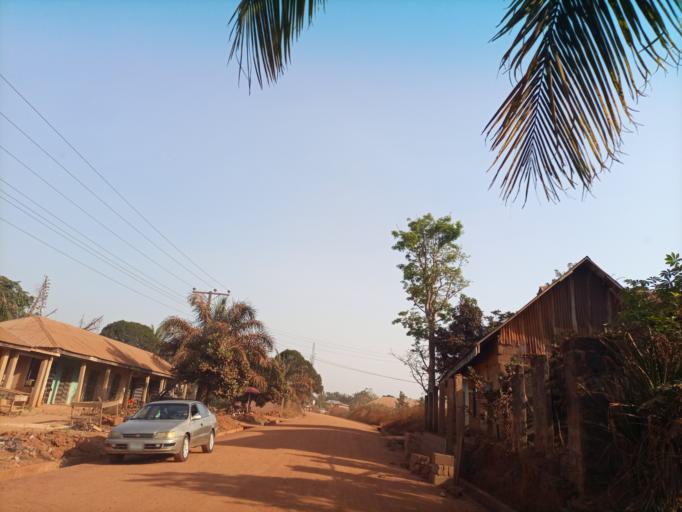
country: NG
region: Enugu
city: Opi
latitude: 6.7483
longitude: 7.4105
